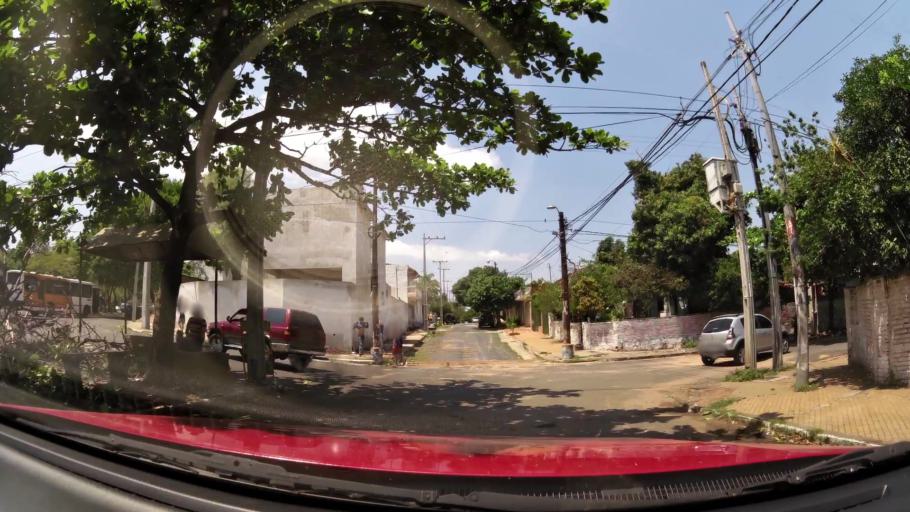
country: PY
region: Asuncion
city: Asuncion
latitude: -25.3004
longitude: -57.6527
